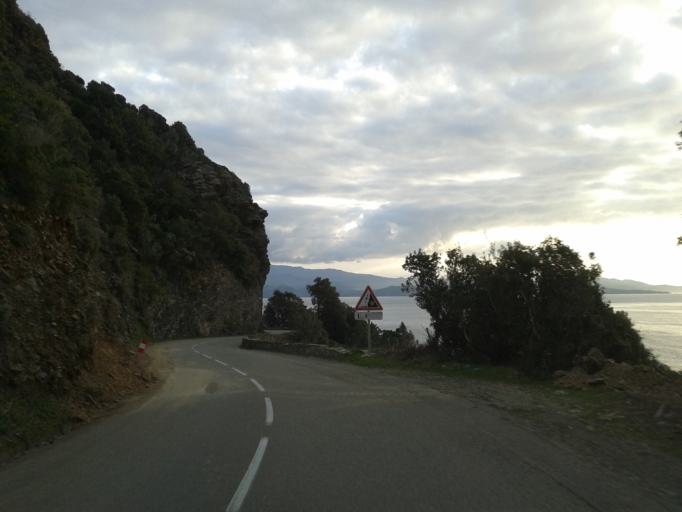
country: FR
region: Corsica
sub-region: Departement de la Haute-Corse
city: Saint-Florent
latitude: 42.7654
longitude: 9.3387
